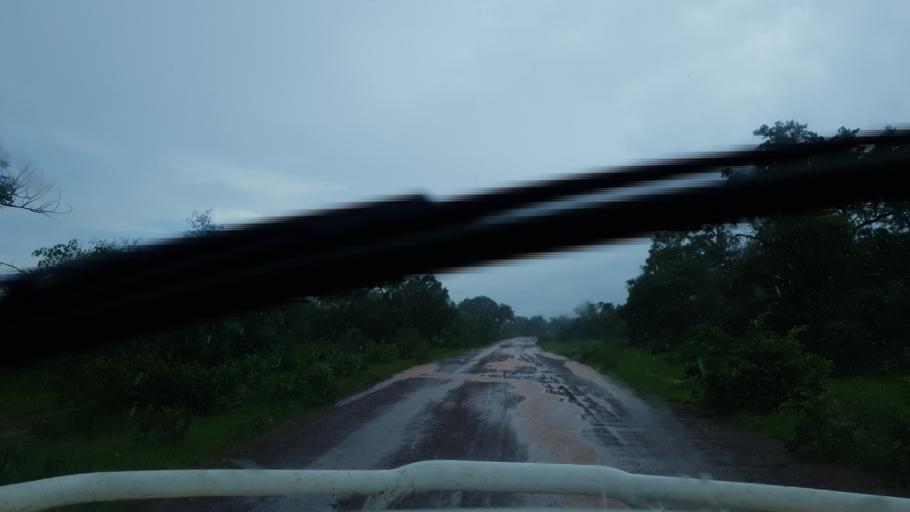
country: ML
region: Sikasso
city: Kolondieba
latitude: 11.6015
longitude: -6.6708
